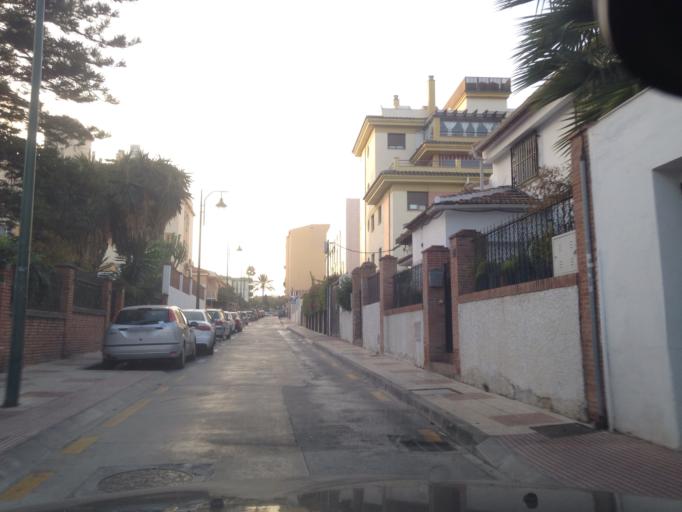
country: ES
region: Andalusia
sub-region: Provincia de Malaga
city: Malaga
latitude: 36.7227
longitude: -4.4534
